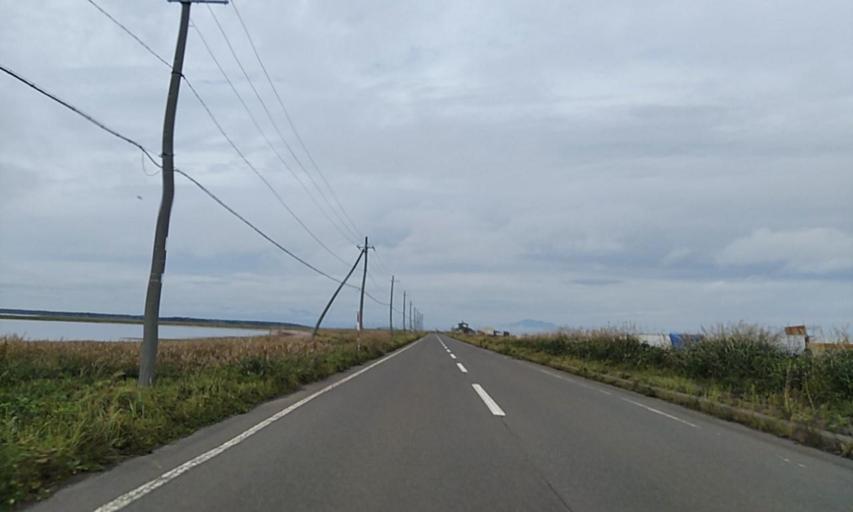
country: JP
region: Hokkaido
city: Shibetsu
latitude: 43.5939
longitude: 145.3287
